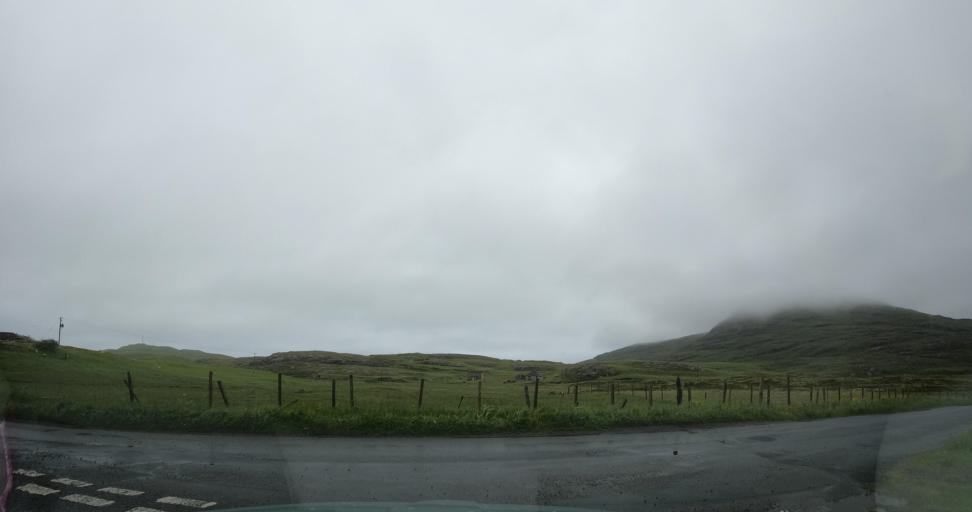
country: GB
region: Scotland
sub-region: Eilean Siar
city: Barra
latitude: 57.0012
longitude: -7.4834
